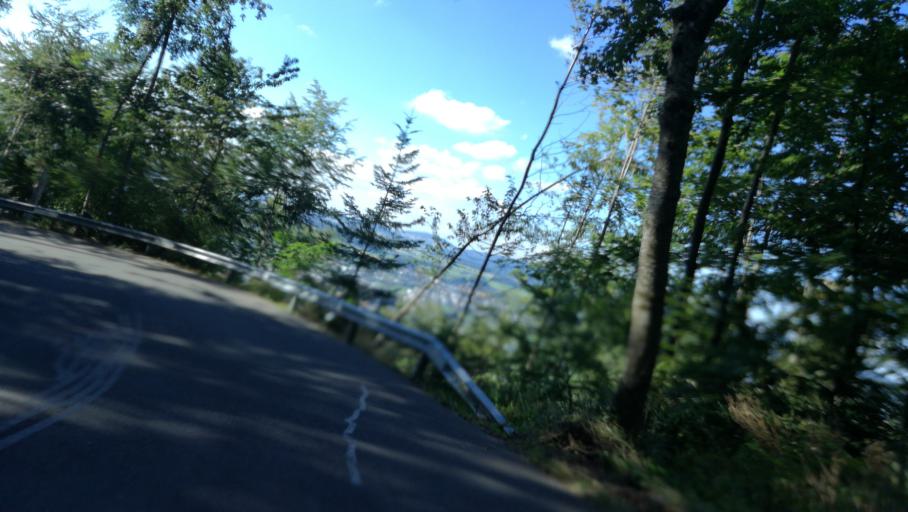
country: CH
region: Zug
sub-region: Zug
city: Zug
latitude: 47.1620
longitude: 8.5311
